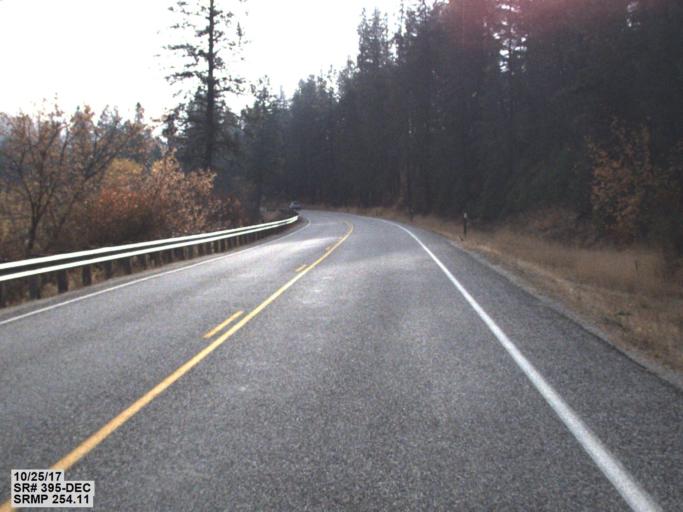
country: US
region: Washington
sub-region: Stevens County
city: Kettle Falls
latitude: 48.7900
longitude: -118.1571
